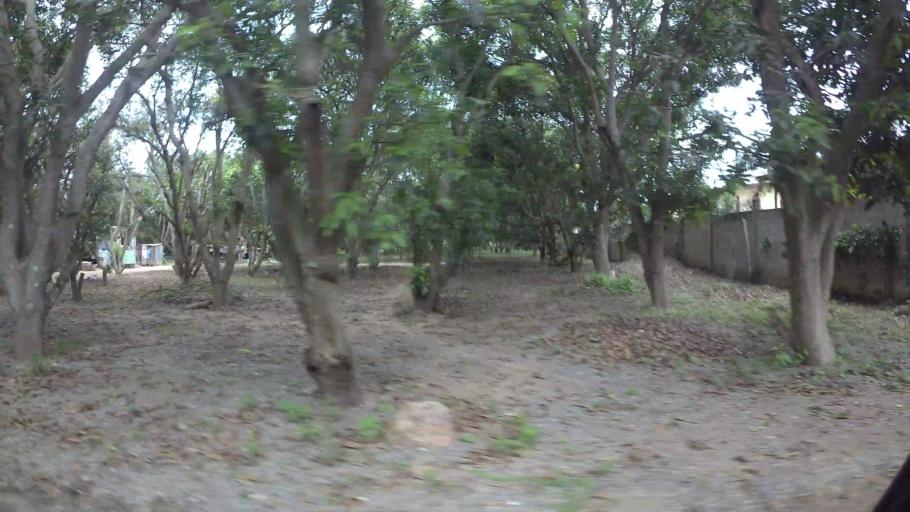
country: TH
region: Chon Buri
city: Sattahip
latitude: 12.6799
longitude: 100.9079
